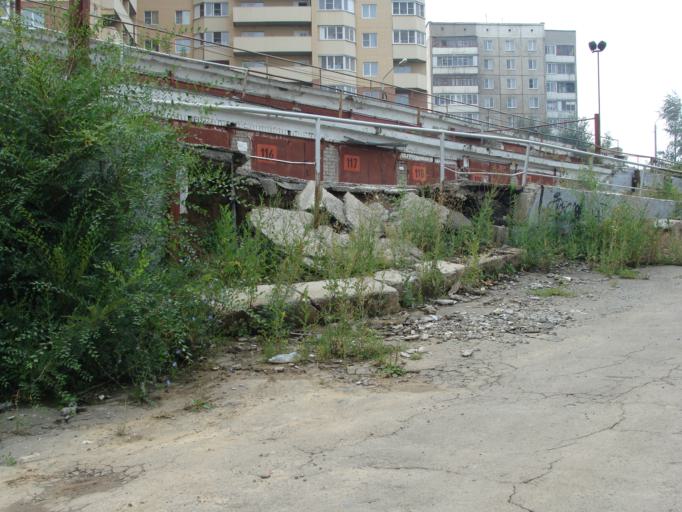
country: RU
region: Altai Krai
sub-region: Gorod Barnaulskiy
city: Barnaul
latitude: 53.3803
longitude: 83.6803
